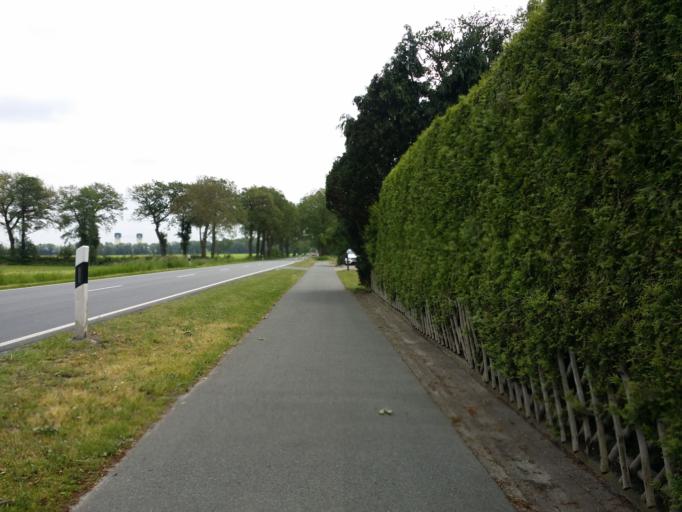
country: DE
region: Lower Saxony
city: Friedeburg
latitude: 53.4222
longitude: 7.8690
